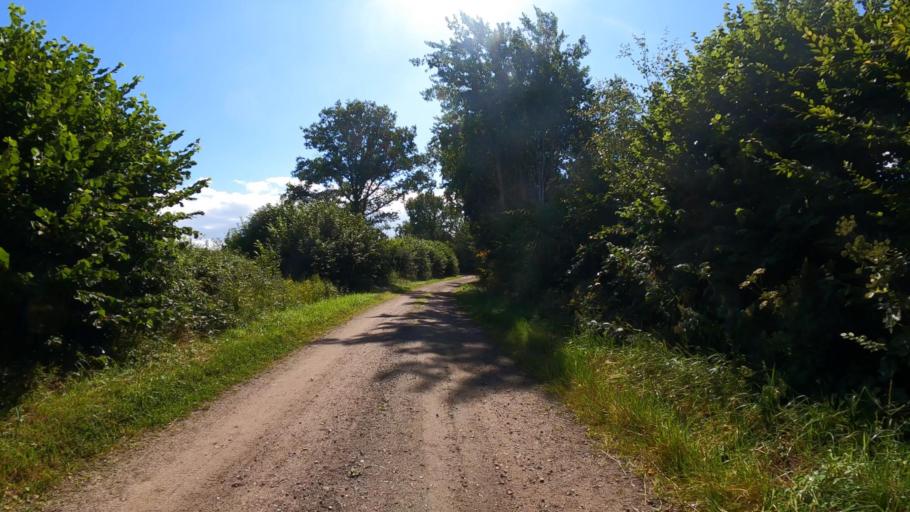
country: DE
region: Schleswig-Holstein
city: Fuhlendorf
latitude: 53.9546
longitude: 9.8846
